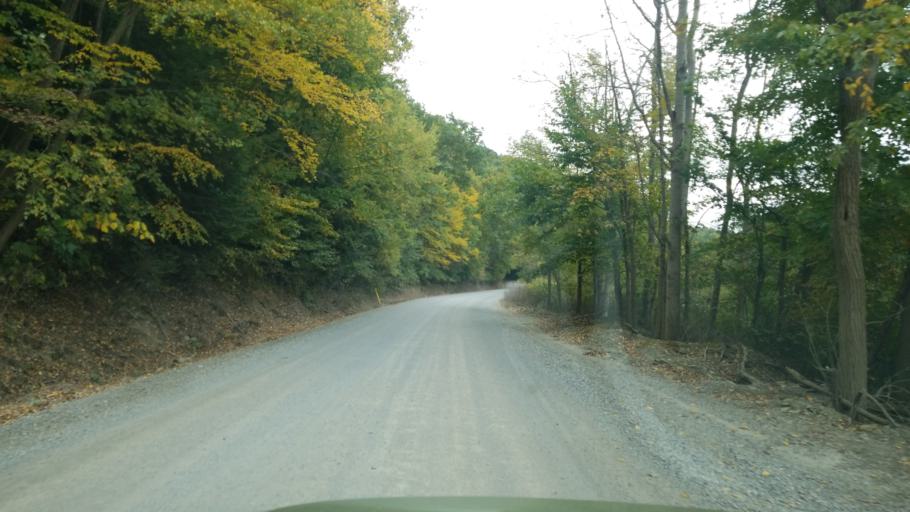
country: US
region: Pennsylvania
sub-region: Clearfield County
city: Curwensville
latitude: 40.9704
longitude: -78.4884
